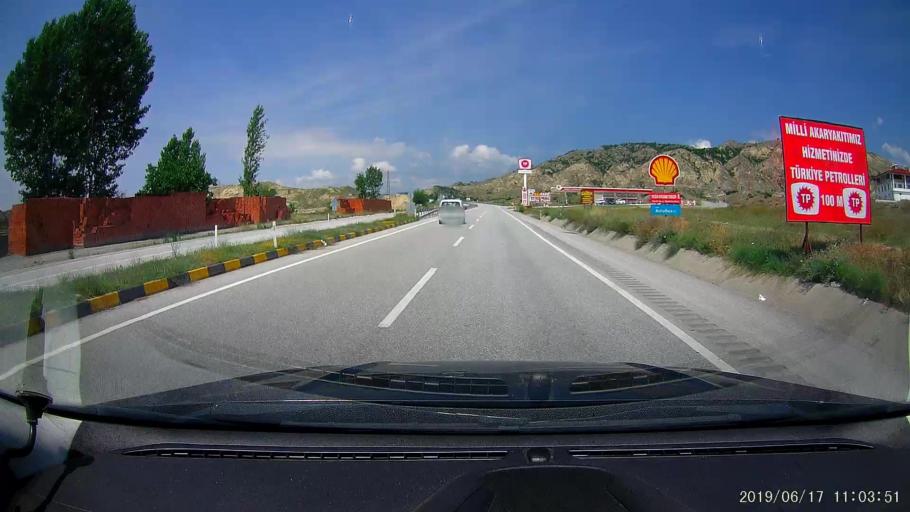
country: TR
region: Kastamonu
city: Tosya
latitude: 41.0197
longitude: 34.1080
